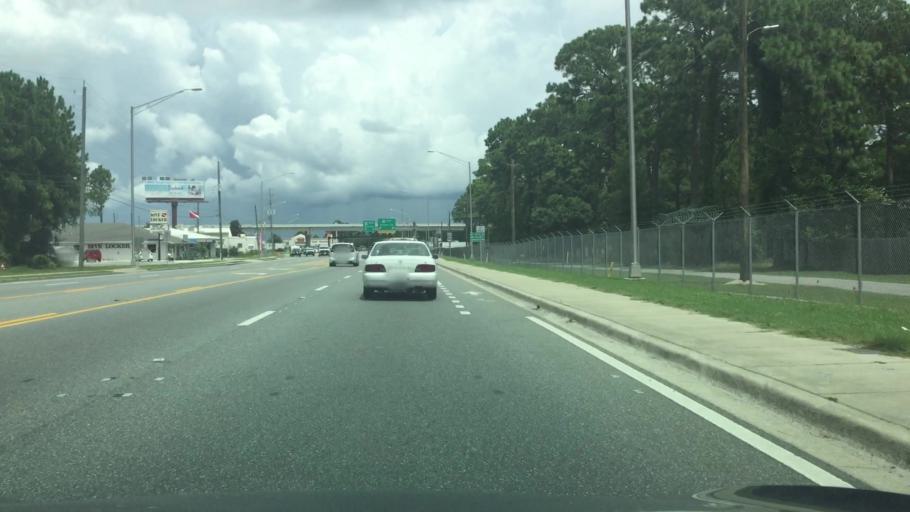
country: US
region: Florida
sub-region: Bay County
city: Upper Grand Lagoon
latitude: 30.1848
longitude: -85.7608
